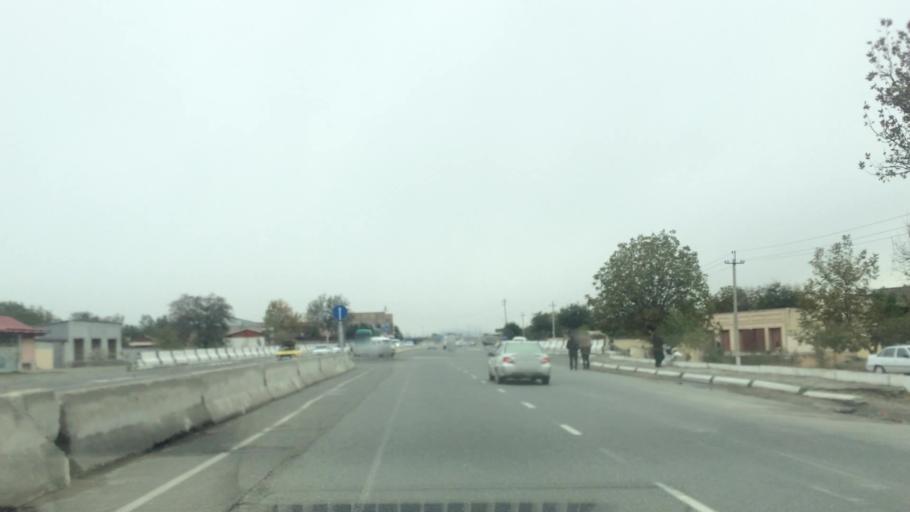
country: UZ
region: Samarqand
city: Jomboy
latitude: 39.6996
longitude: 67.0751
